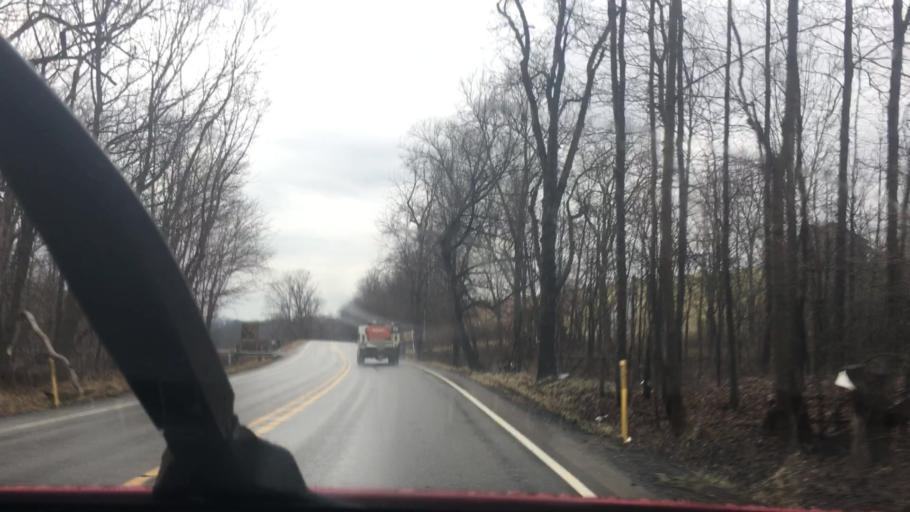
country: US
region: Pennsylvania
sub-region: Washington County
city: McDonald
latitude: 40.3393
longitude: -80.2396
